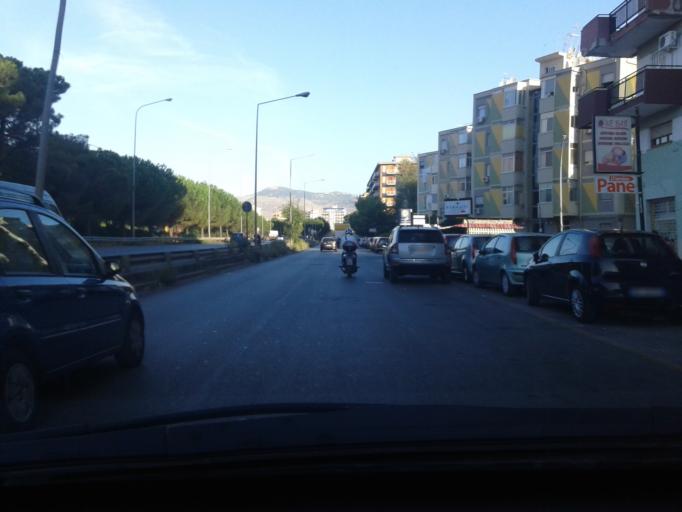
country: IT
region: Sicily
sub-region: Palermo
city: Palermo
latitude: 38.0979
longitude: 13.3343
